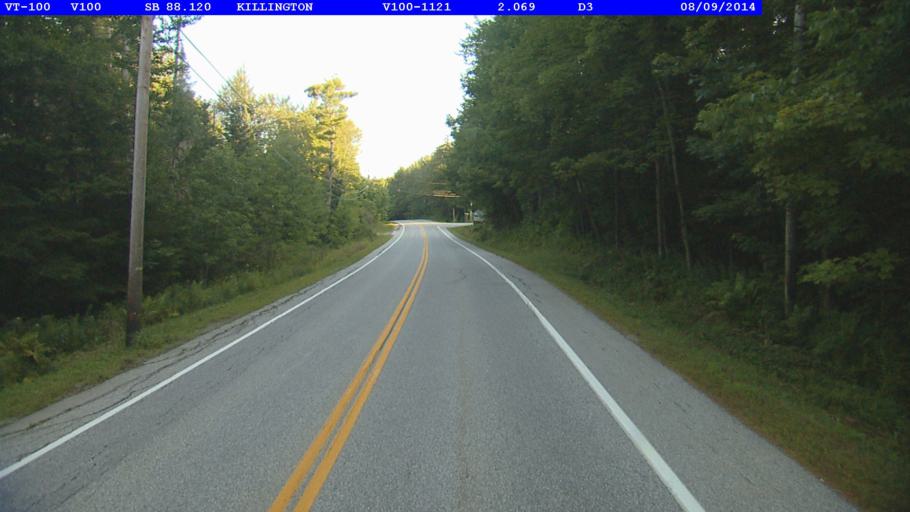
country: US
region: Vermont
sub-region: Rutland County
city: Rutland
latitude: 43.6950
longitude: -72.8143
